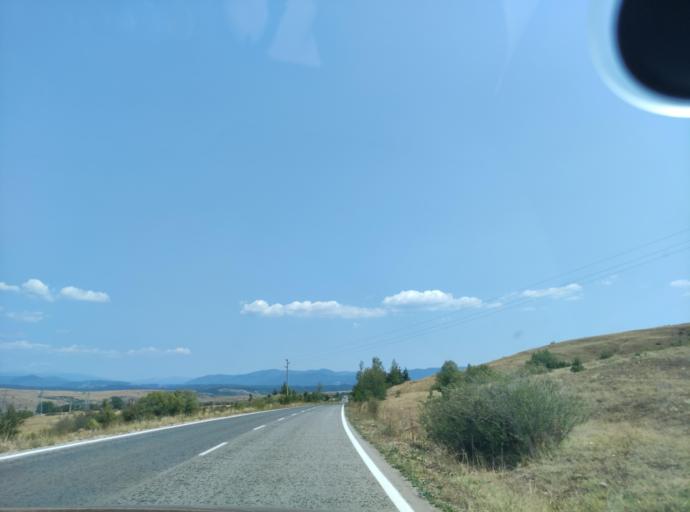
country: BG
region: Blagoevgrad
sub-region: Obshtina Razlog
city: Razlog
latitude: 41.8799
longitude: 23.4848
